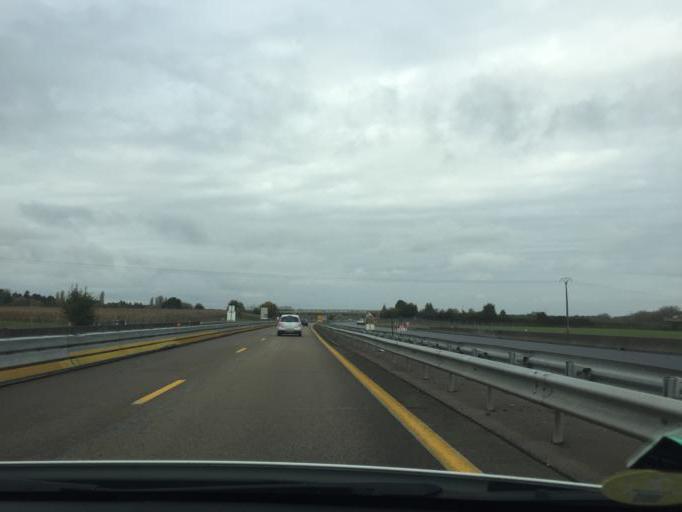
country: FR
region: Bourgogne
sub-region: Departement de l'Yonne
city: Saint-Julien-du-Sault
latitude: 47.9819
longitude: 3.1885
